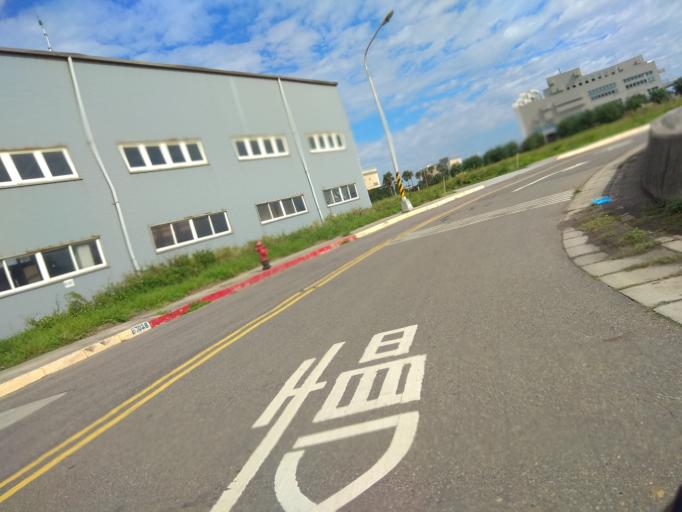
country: TW
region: Taiwan
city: Taoyuan City
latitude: 25.0525
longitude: 121.0949
